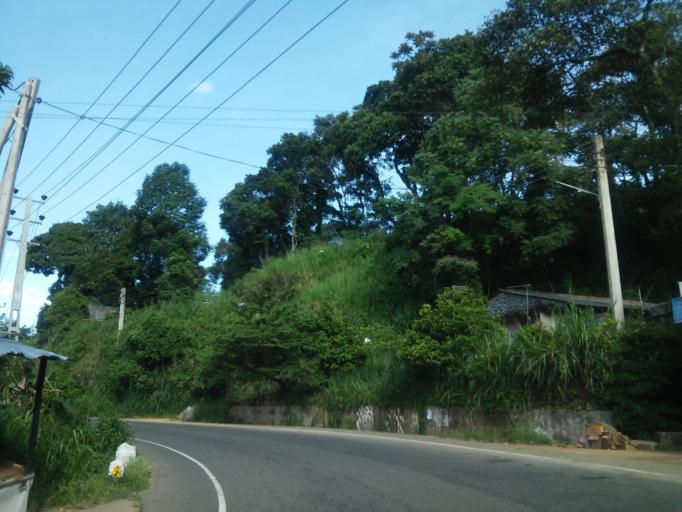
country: LK
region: Uva
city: Haputale
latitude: 6.7609
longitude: 80.8817
